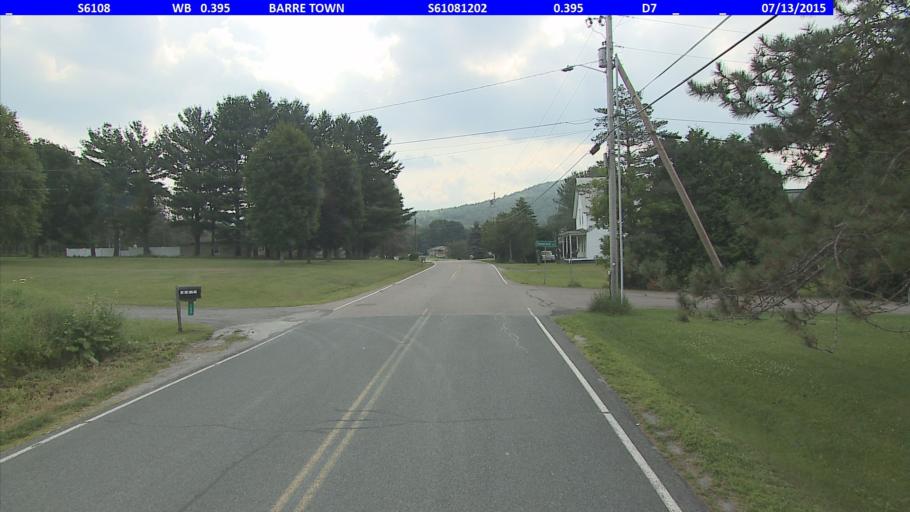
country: US
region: Vermont
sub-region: Washington County
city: Barre
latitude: 44.1854
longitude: -72.4737
